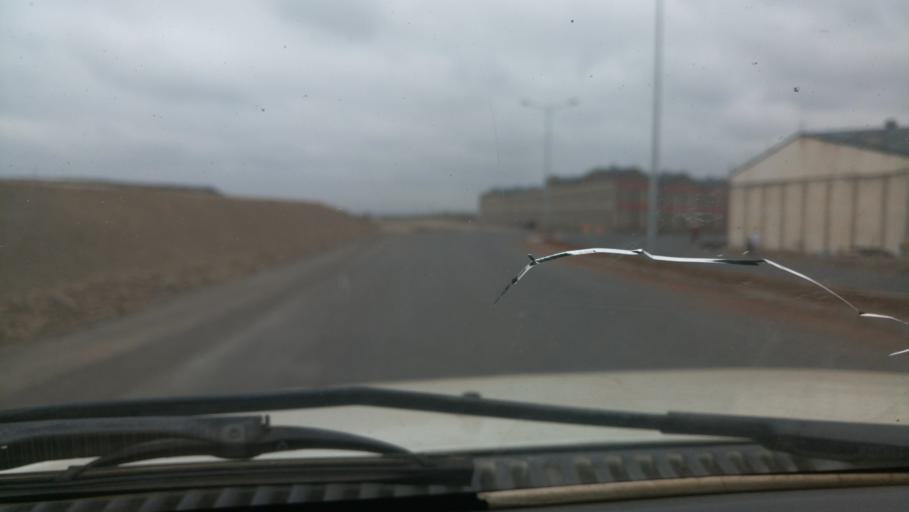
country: KE
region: Nairobi Area
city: Pumwani
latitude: -1.3442
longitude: 36.8839
